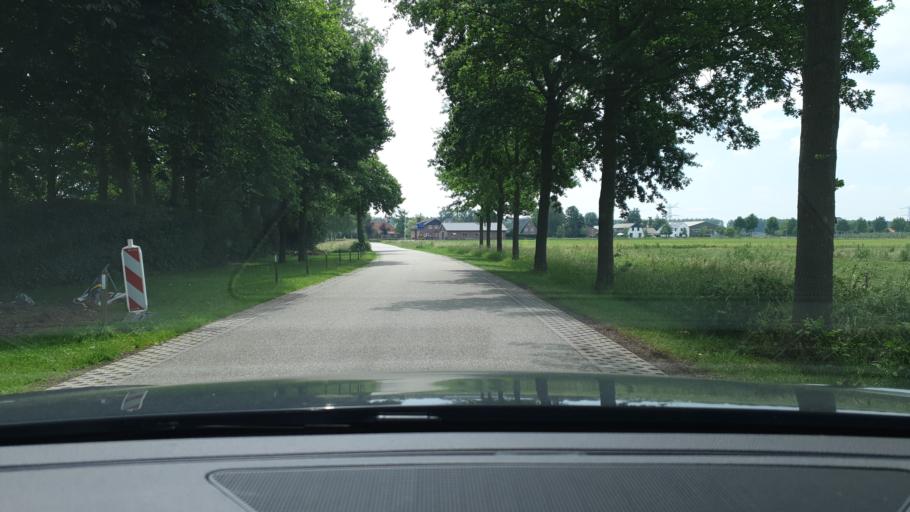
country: NL
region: Gelderland
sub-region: Gemeente Overbetuwe
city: Elst
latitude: 51.9081
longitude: 5.8916
